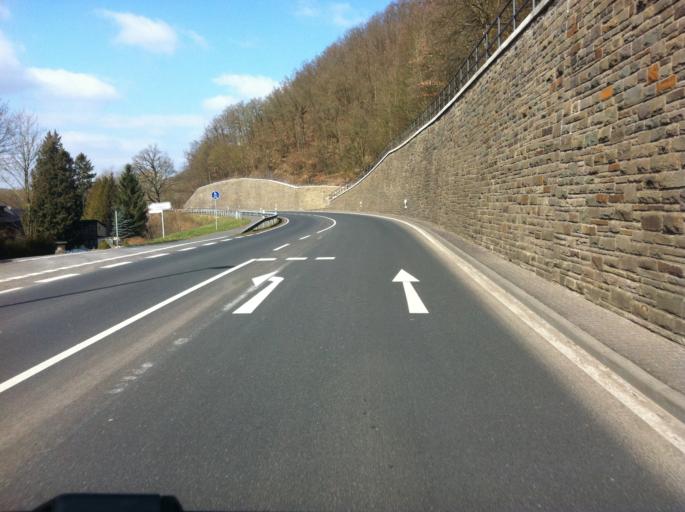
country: DE
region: North Rhine-Westphalia
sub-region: Regierungsbezirk Koln
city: Bad Munstereifel
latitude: 50.5381
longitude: 6.7690
